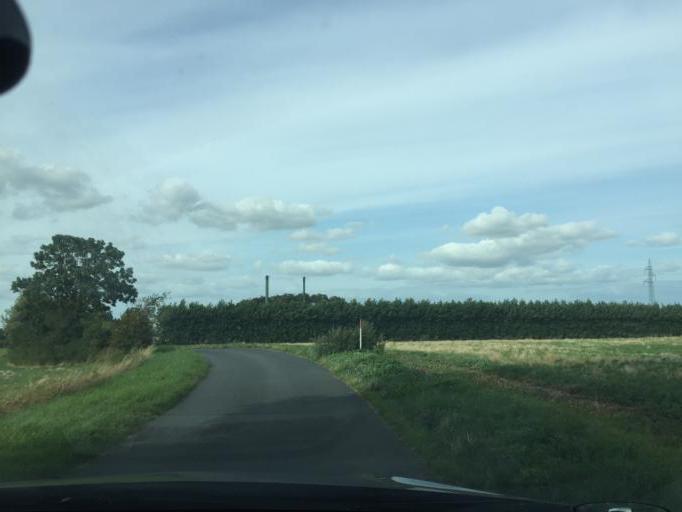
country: DK
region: South Denmark
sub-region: Faaborg-Midtfyn Kommune
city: Arslev
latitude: 55.3439
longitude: 10.5131
